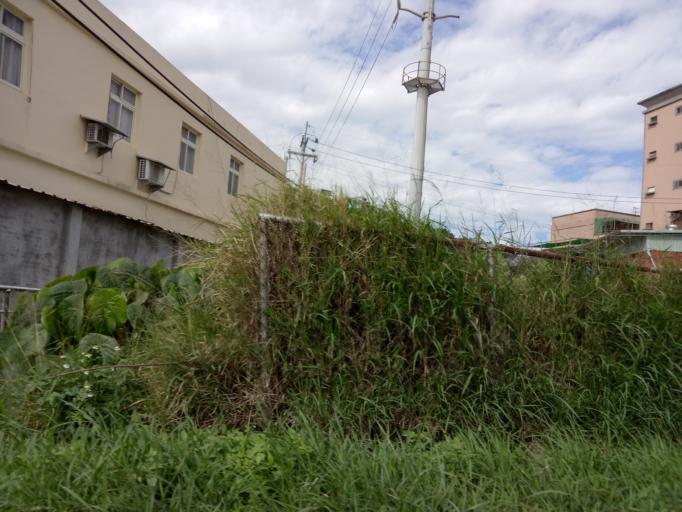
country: TW
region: Taiwan
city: Daxi
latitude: 24.8966
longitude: 121.2882
